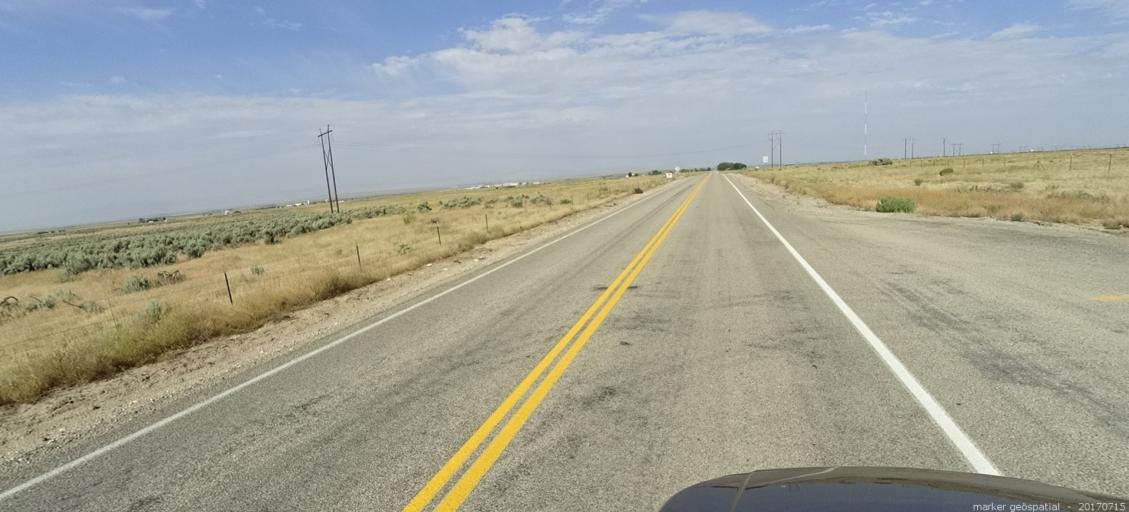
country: US
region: Idaho
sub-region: Ada County
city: Boise
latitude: 43.4587
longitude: -116.2357
